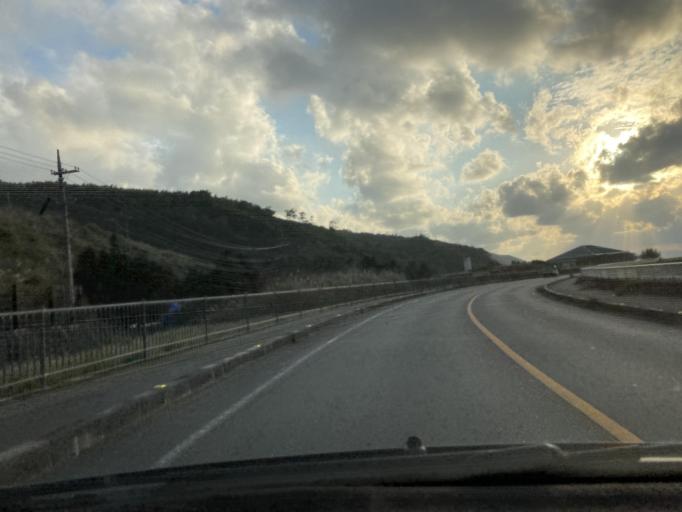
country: JP
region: Okinawa
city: Nago
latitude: 26.7886
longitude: 128.2237
